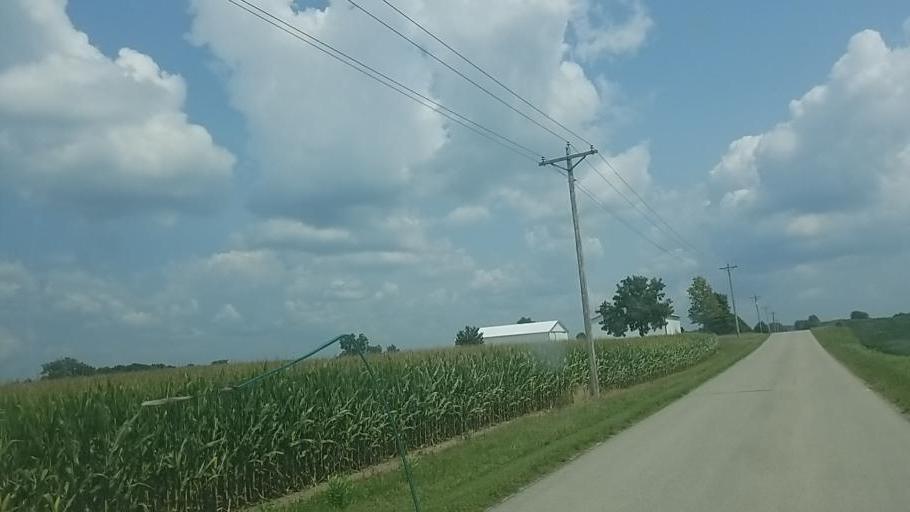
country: US
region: Ohio
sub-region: Wyandot County
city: Upper Sandusky
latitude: 40.9209
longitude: -83.1622
